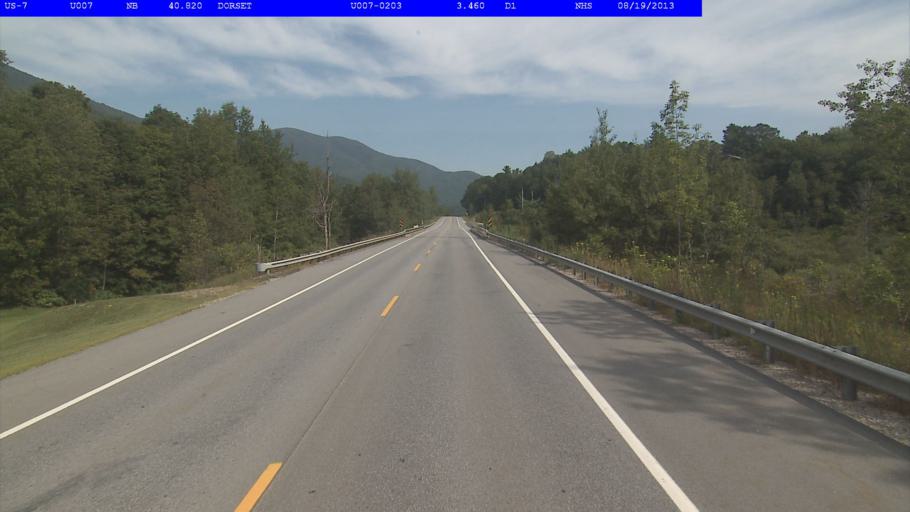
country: US
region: Vermont
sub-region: Bennington County
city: Manchester Center
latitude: 43.2591
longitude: -73.0080
